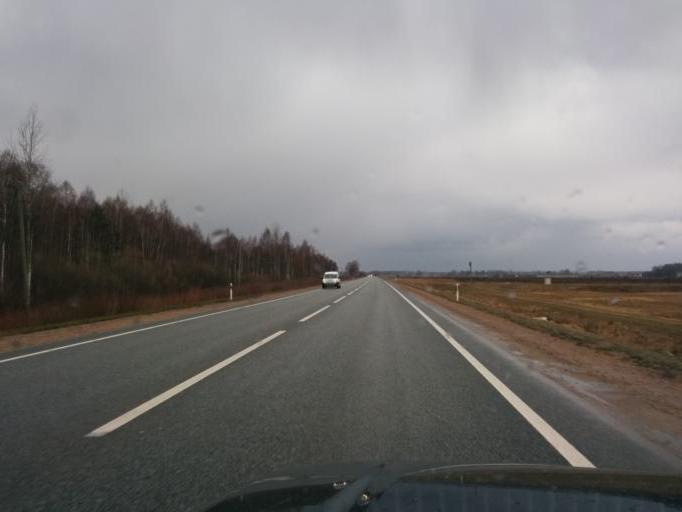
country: LV
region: Marupe
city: Marupe
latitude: 56.8594
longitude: 23.9899
